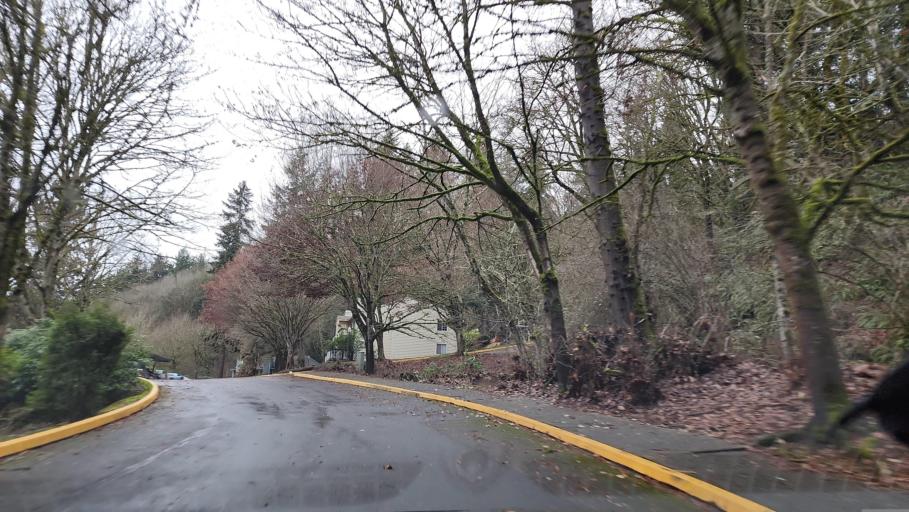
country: US
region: Washington
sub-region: King County
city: Redmond
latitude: 47.6812
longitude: -122.1067
